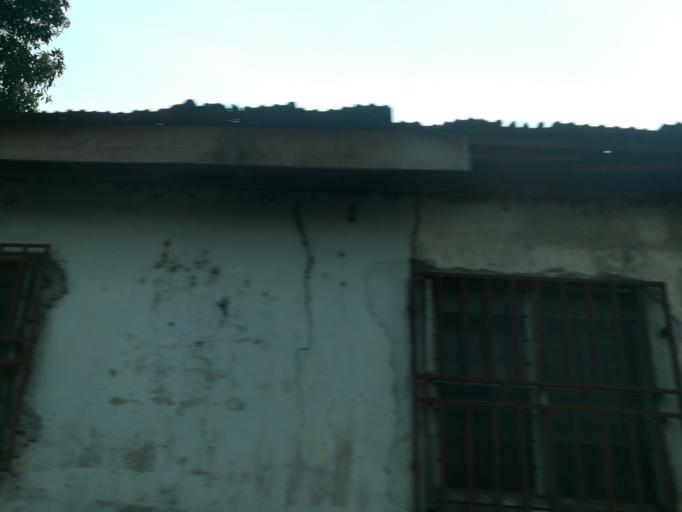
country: NG
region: Rivers
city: Port Harcourt
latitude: 4.8109
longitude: 7.0209
